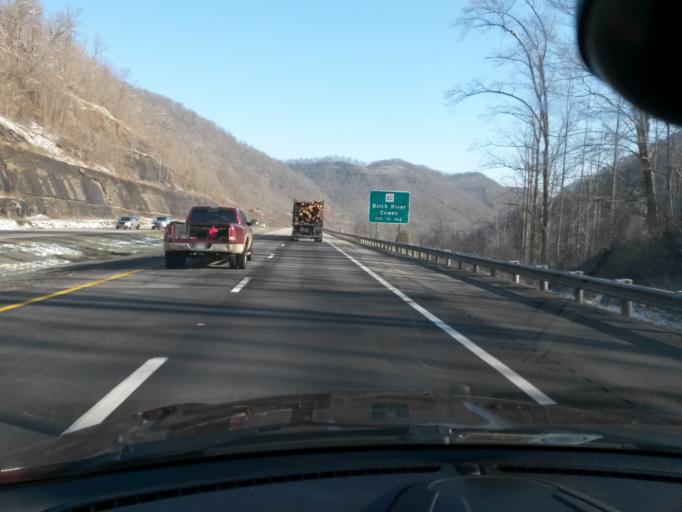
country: US
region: West Virginia
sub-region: Braxton County
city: Sutton
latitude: 38.4878
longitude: -80.7582
